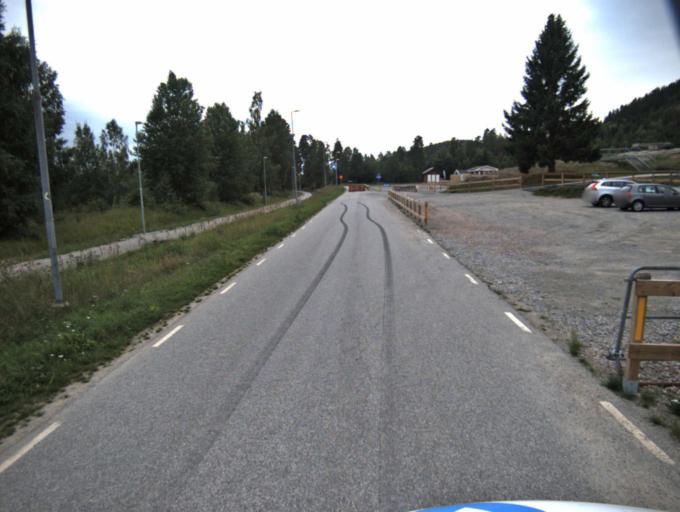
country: SE
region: Vaestra Goetaland
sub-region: Ulricehamns Kommun
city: Ulricehamn
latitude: 57.8201
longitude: 13.4131
